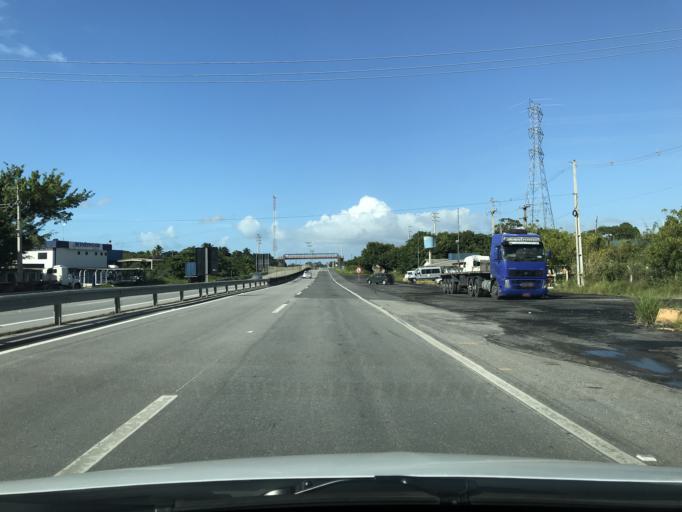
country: BR
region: Pernambuco
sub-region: Ipojuca
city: Ipojuca
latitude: -8.3975
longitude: -35.0117
